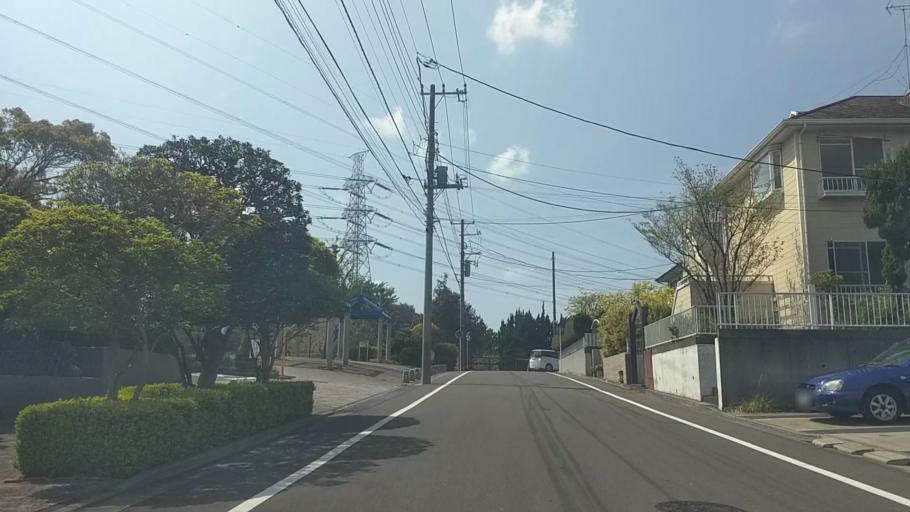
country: JP
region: Kanagawa
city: Kamakura
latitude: 35.3697
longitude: 139.5755
